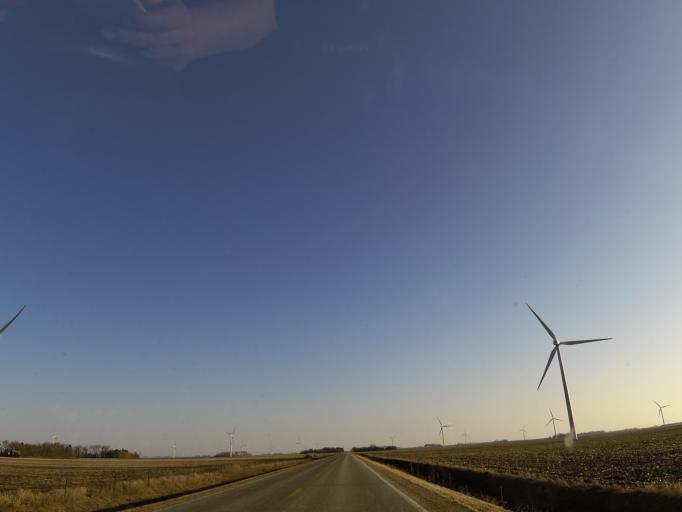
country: US
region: Iowa
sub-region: Worth County
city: Northwood
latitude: 43.4255
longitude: -93.1244
